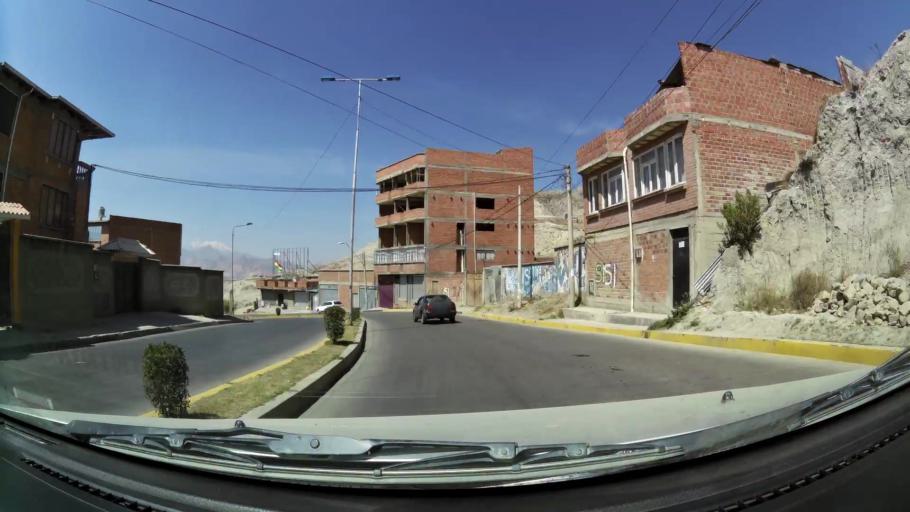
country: BO
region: La Paz
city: La Paz
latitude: -16.5312
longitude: -68.1274
